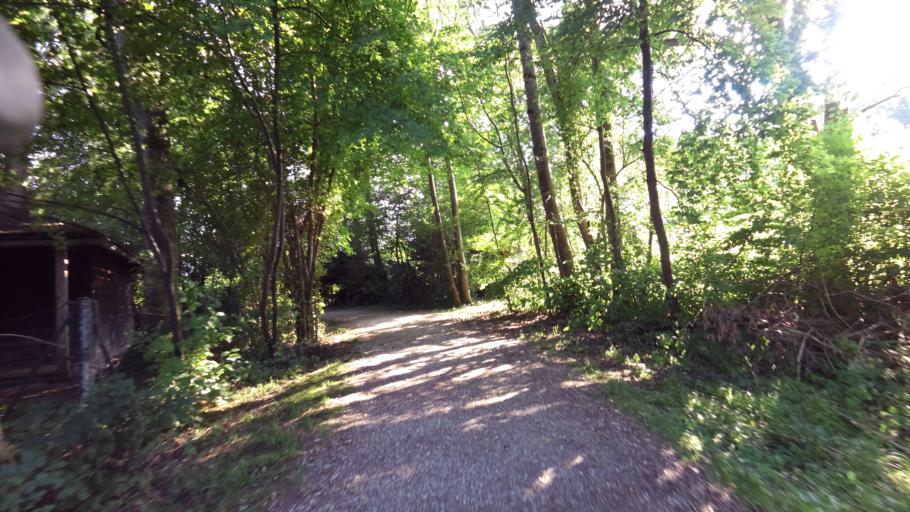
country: DE
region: Bavaria
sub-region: Upper Bavaria
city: Gstadt am Chiemsee
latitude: 47.8787
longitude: 12.3894
